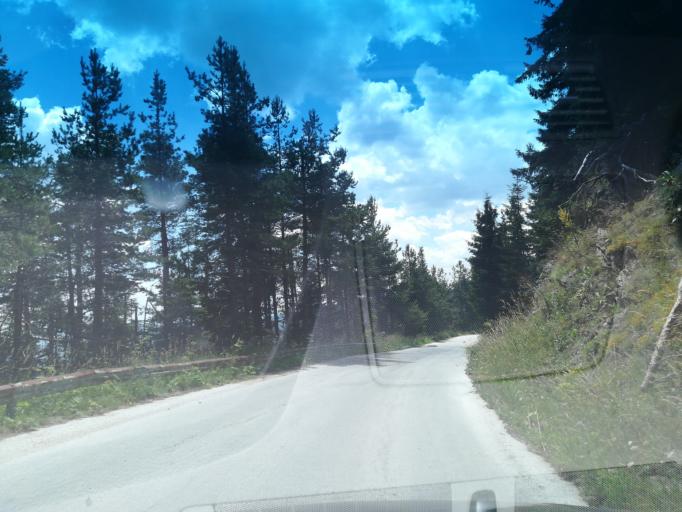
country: BG
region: Smolyan
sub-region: Obshtina Chepelare
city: Chepelare
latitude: 41.6877
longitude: 24.7578
